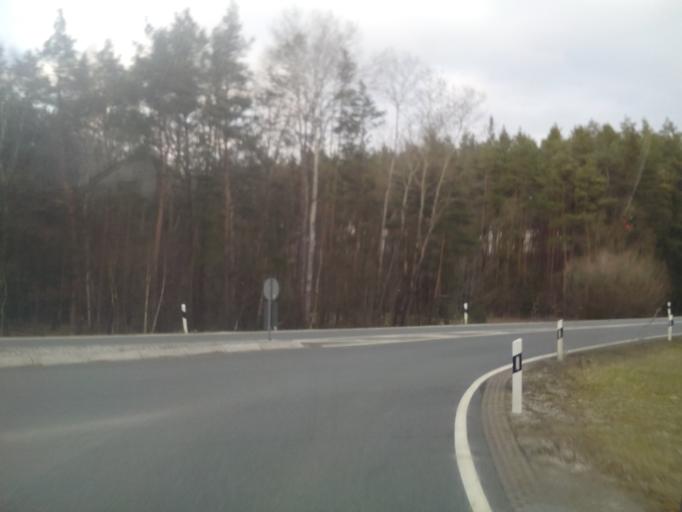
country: DE
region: Bavaria
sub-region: Upper Franconia
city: Pommersfelden
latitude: 49.7434
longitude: 10.8173
